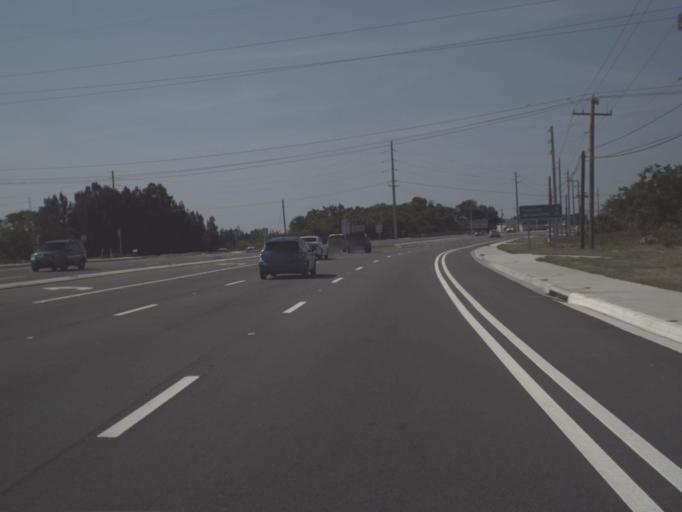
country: US
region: Florida
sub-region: Brevard County
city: Cocoa
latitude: 28.4037
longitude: -80.7545
